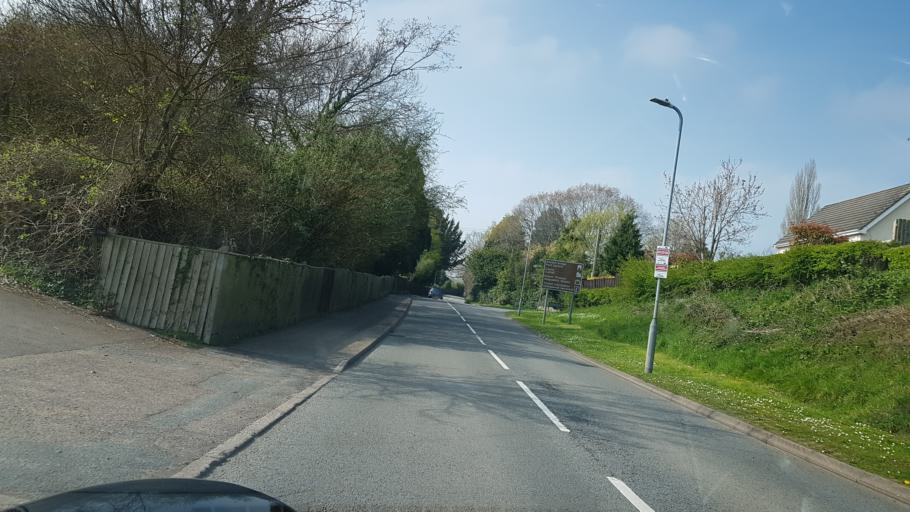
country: GB
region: Wales
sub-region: Monmouthshire
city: Monmouth
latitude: 51.8048
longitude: -2.7032
